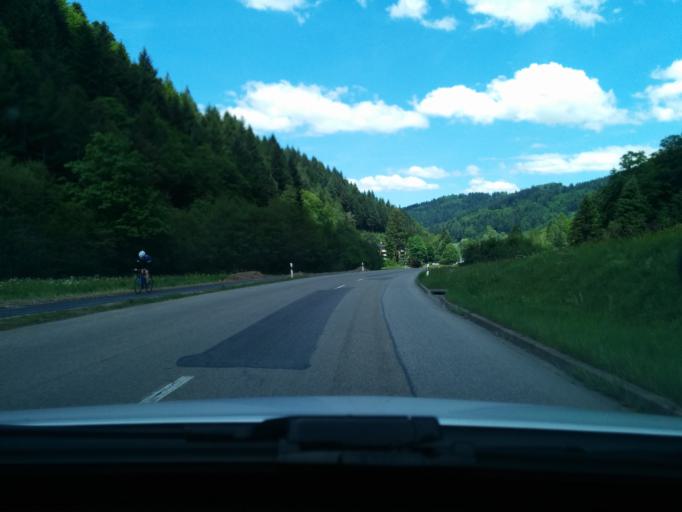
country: DE
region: Baden-Wuerttemberg
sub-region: Freiburg Region
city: Horben
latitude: 47.9525
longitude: 7.8649
